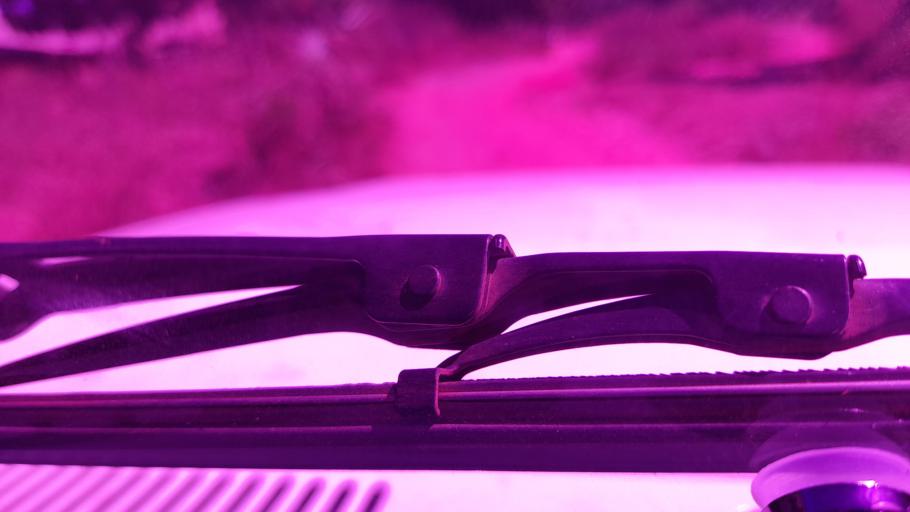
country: GW
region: Oio
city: Bissora
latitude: 12.4029
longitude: -15.7028
